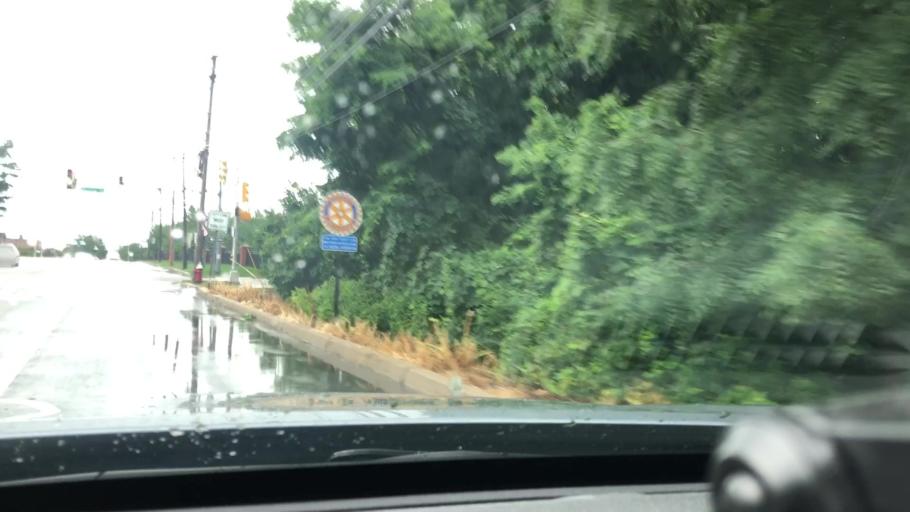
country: US
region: New Jersey
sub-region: Bergen County
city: Woodcliff Lake
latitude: 41.0397
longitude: -74.0769
